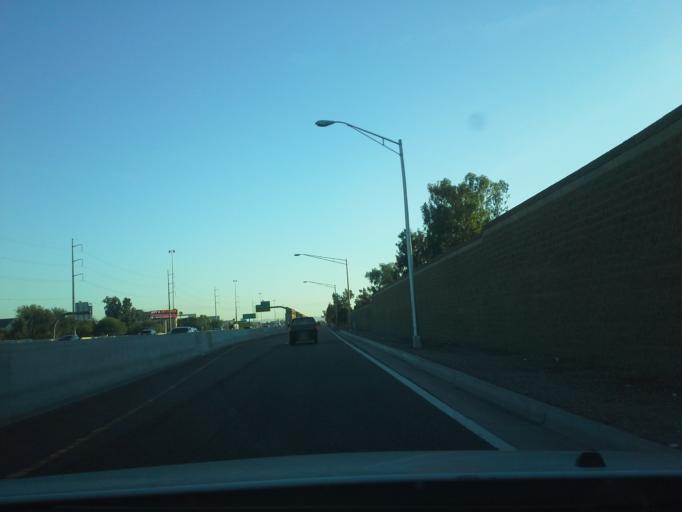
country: US
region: Arizona
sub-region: Maricopa County
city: Glendale
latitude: 33.5924
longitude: -112.1173
